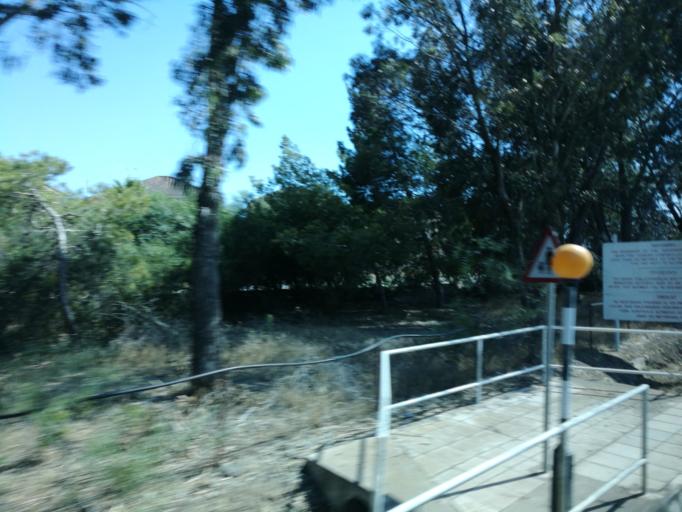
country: CY
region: Ammochostos
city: Acheritou
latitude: 35.0804
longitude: 33.8720
